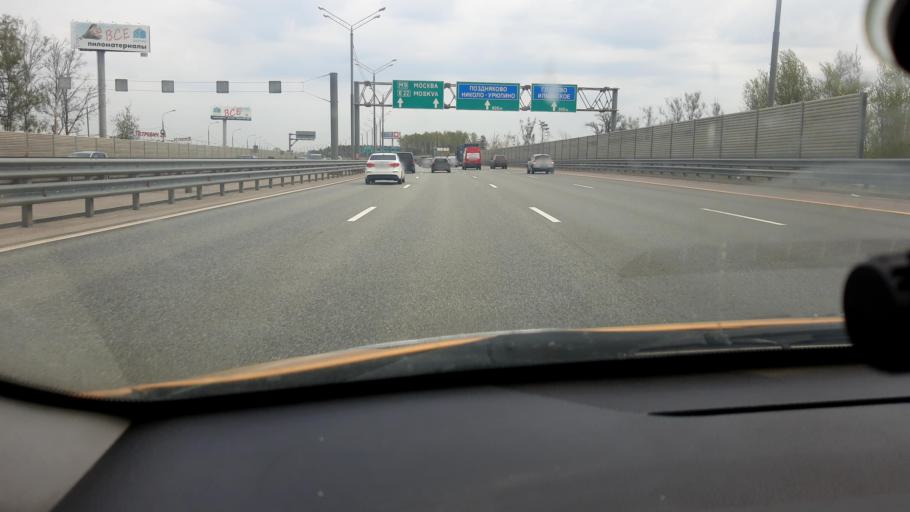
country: RU
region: Moskovskaya
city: Opalikha
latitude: 55.7765
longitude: 37.2303
